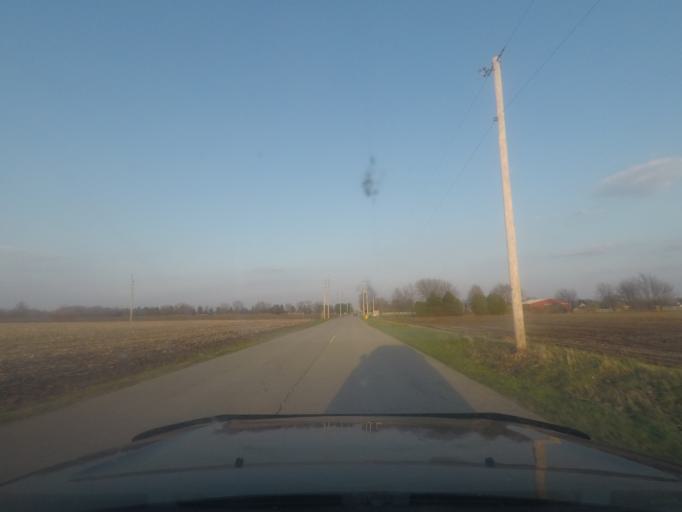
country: US
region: Indiana
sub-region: LaPorte County
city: LaPorte
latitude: 41.5692
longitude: -86.7213
